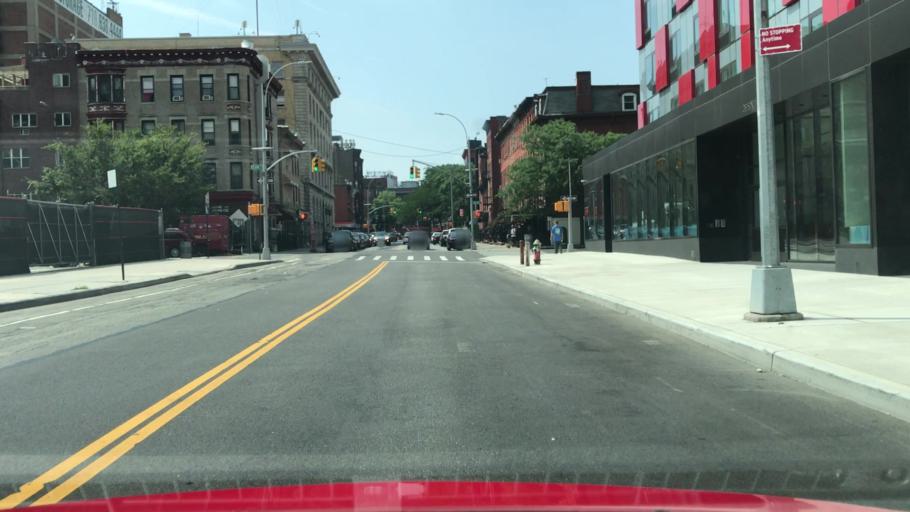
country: US
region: New York
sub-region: Kings County
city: Brooklyn
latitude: 40.6820
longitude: -73.9741
